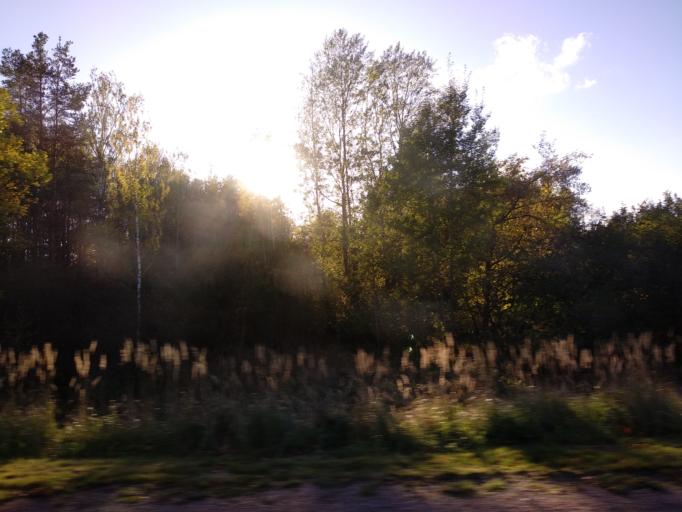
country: EE
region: Polvamaa
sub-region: Polva linn
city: Polva
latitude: 58.0490
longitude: 27.0635
